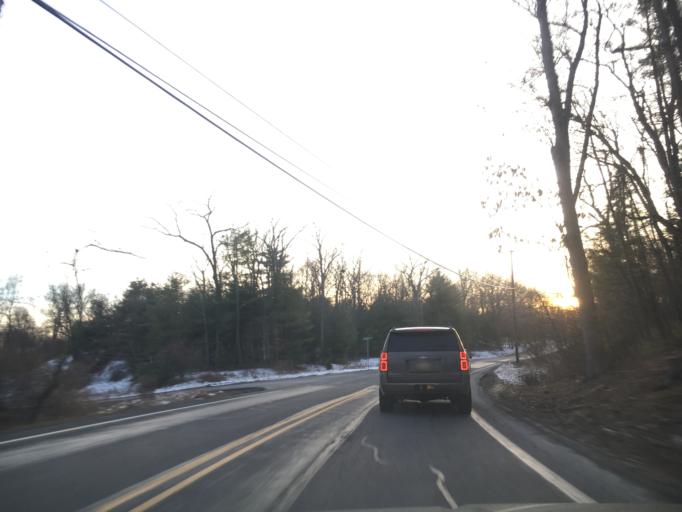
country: US
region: Pennsylvania
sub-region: Pike County
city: Saw Creek
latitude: 41.0610
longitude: -75.1155
